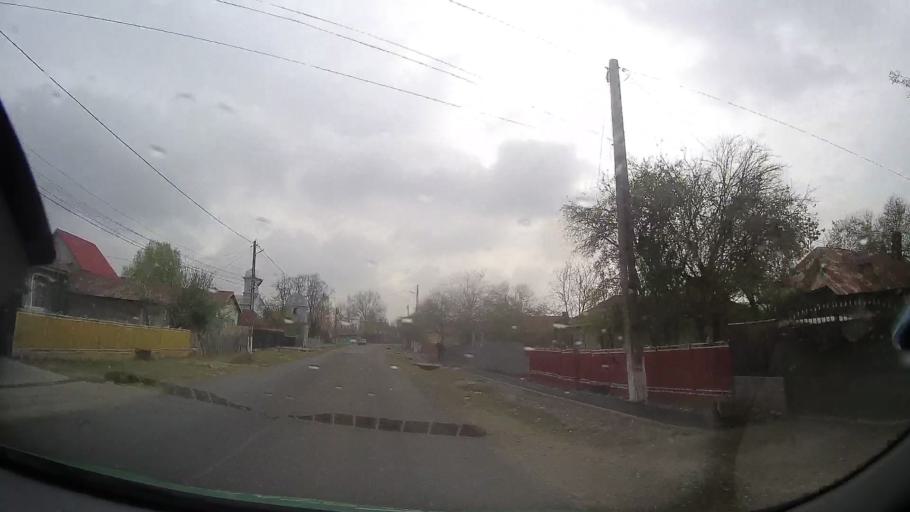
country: RO
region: Prahova
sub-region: Comuna Draganesti
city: Draganesti
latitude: 44.8416
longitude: 26.2692
